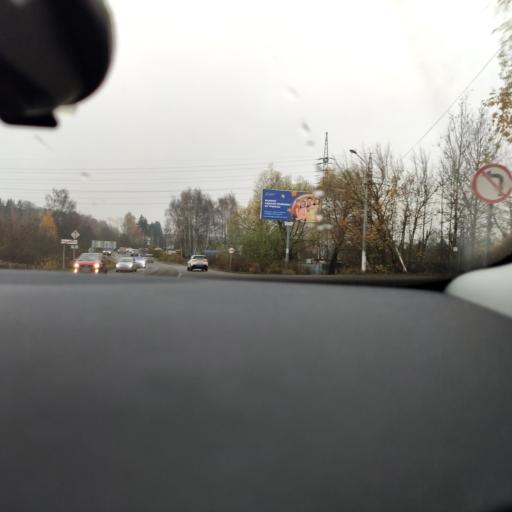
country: RU
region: Moskovskaya
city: Nakhabino
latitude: 55.8347
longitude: 37.1547
